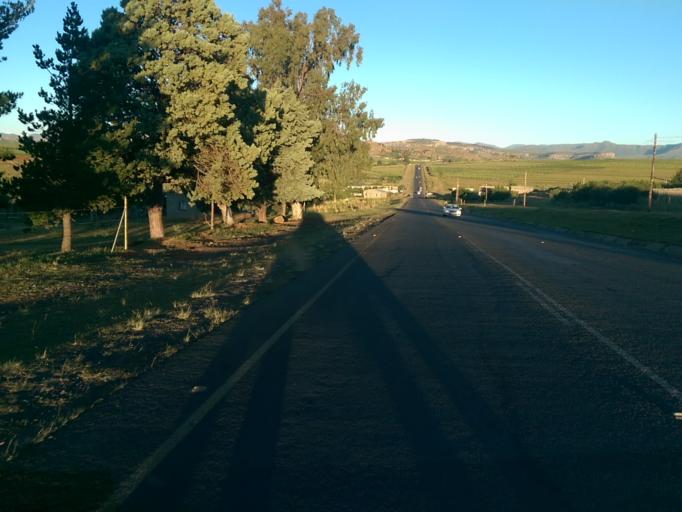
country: LS
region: Maseru
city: Maseru
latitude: -29.4085
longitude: 27.5923
